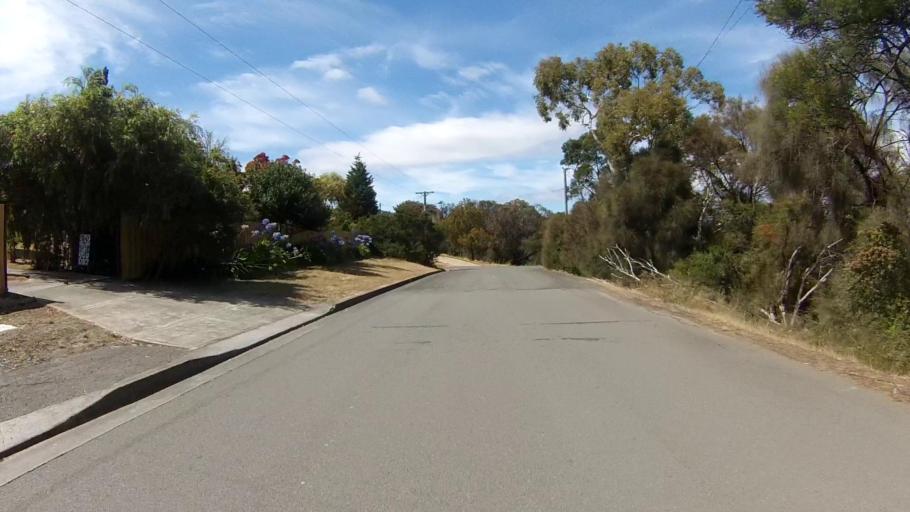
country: AU
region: Tasmania
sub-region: Glenorchy
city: Lutana
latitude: -42.8261
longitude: 147.3204
